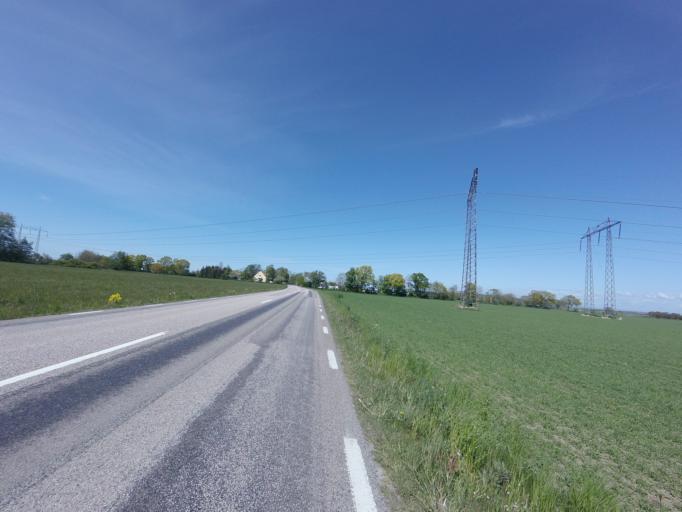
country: SE
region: Skane
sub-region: Helsingborg
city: Odakra
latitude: 56.1357
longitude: 12.6904
